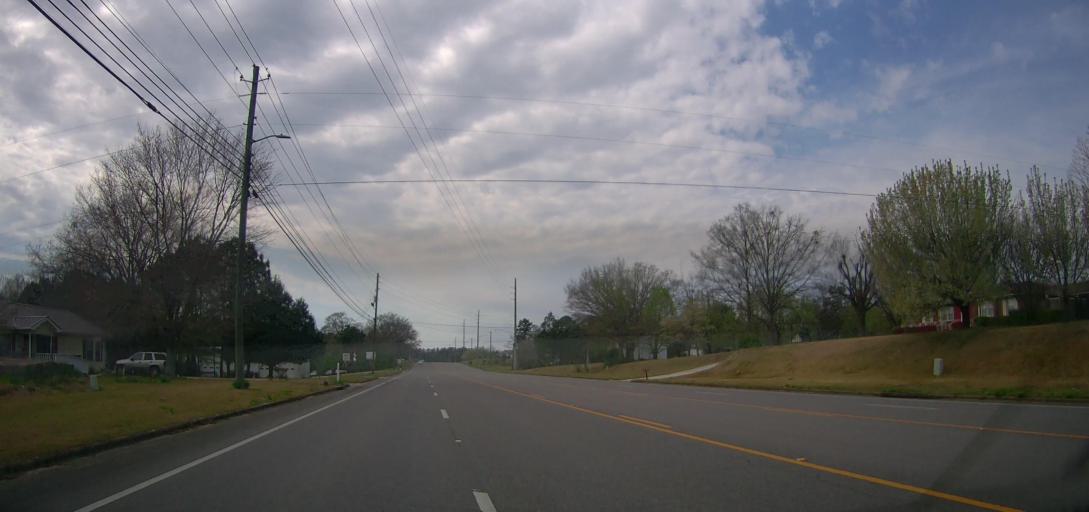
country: US
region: Alabama
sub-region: Marion County
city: Winfield
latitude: 33.9303
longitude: -87.7769
